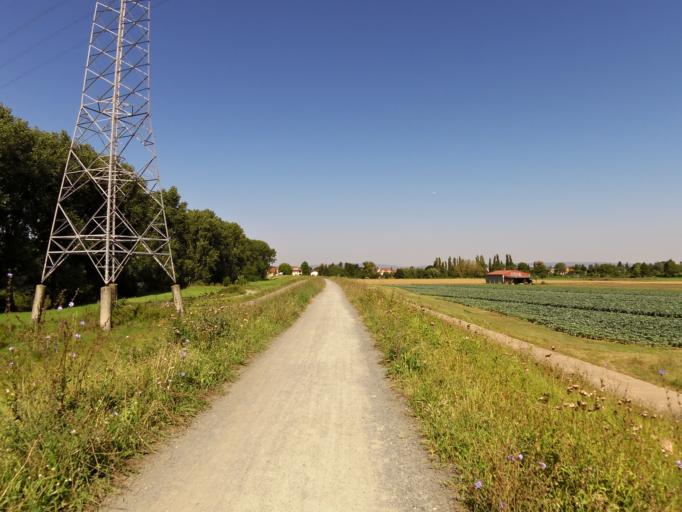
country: DE
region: Hesse
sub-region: Regierungsbezirk Darmstadt
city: Ginsheim-Gustavsburg
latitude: 49.9589
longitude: 8.3554
